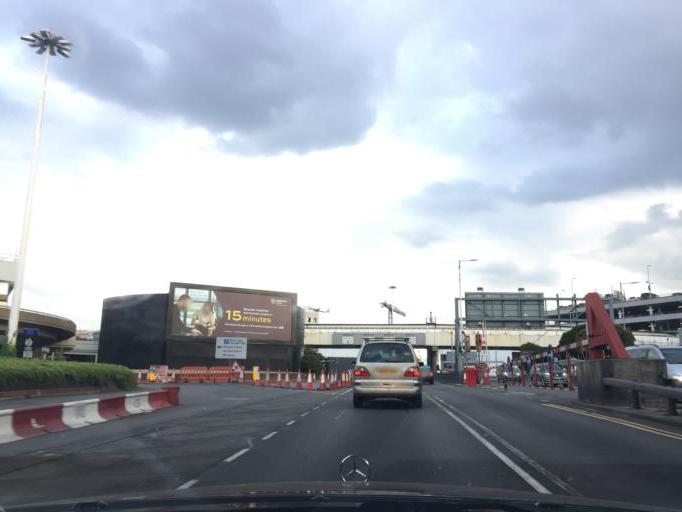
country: GB
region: England
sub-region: Greater London
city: West Drayton
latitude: 51.4738
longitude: -0.4529
